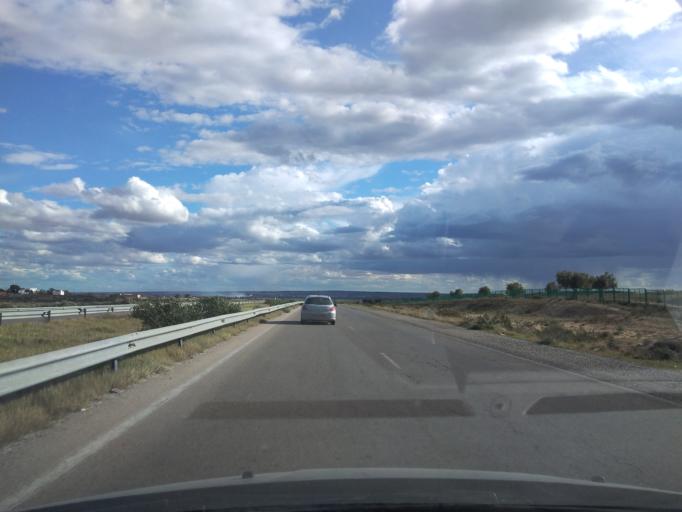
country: TN
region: Al Munastir
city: Manzil Kamil
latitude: 35.5368
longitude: 10.6237
